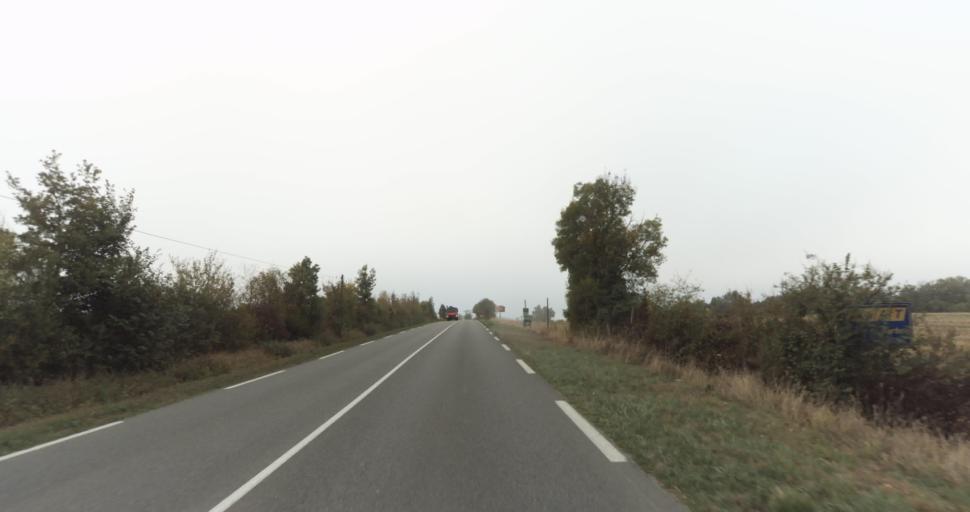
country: FR
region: Midi-Pyrenees
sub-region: Departement du Gers
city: Preignan
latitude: 43.7034
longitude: 0.6161
